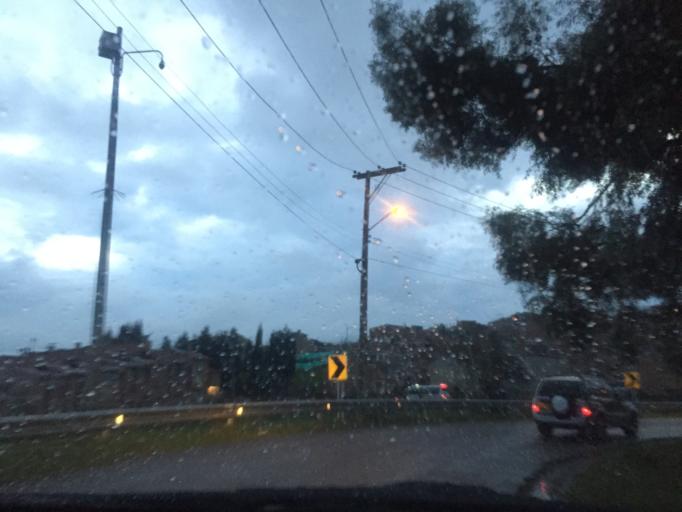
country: CO
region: Cundinamarca
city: Cogua
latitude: 5.0664
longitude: -73.9769
